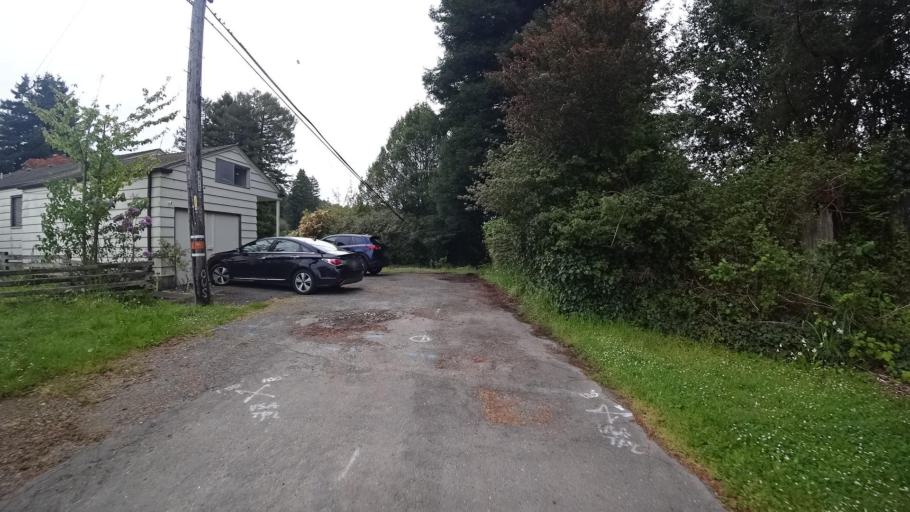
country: US
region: California
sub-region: Humboldt County
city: Blue Lake
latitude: 40.8799
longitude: -123.9857
